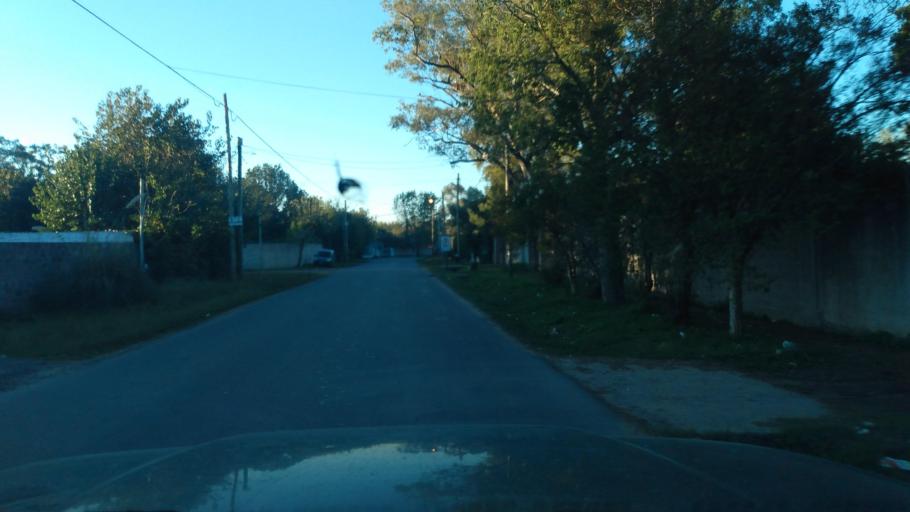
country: AR
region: Buenos Aires
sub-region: Partido de Merlo
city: Merlo
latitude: -34.6586
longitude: -58.7495
